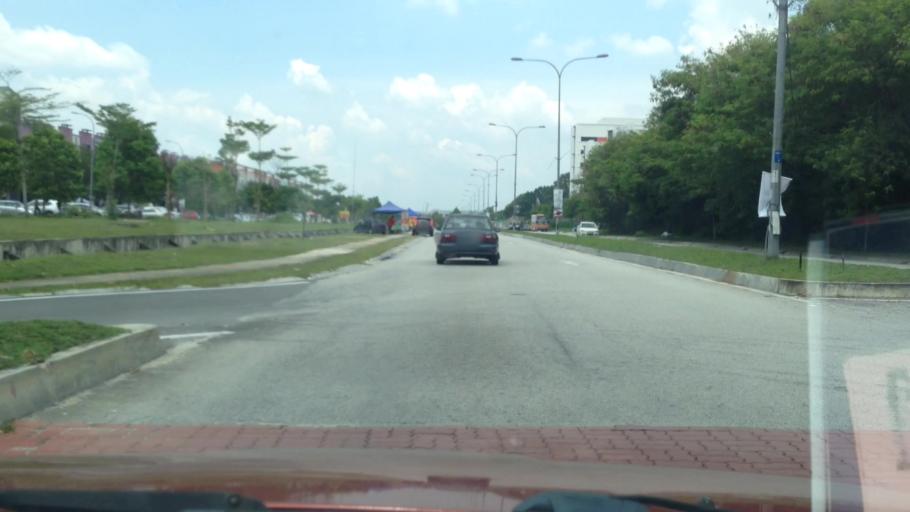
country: MY
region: Selangor
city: Kampung Baru Subang
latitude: 3.1756
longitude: 101.5492
